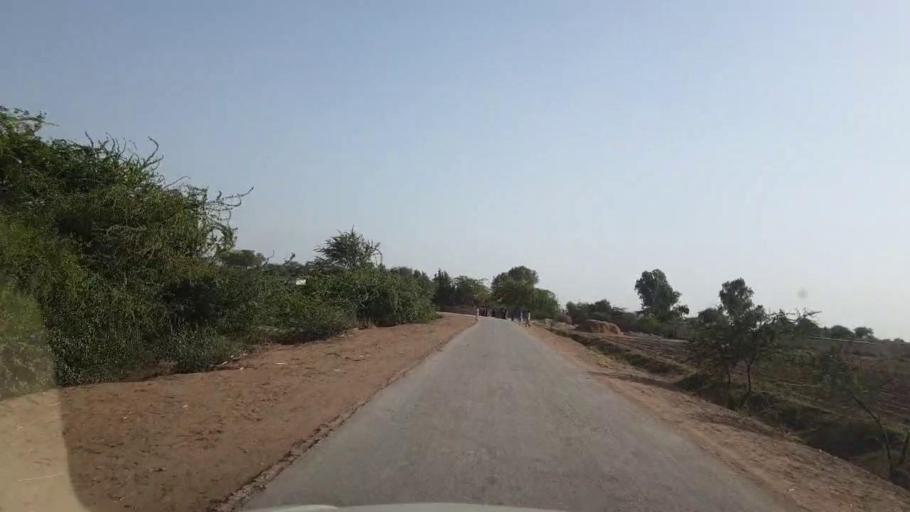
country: PK
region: Sindh
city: Tando Ghulam Ali
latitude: 25.0863
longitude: 68.8689
